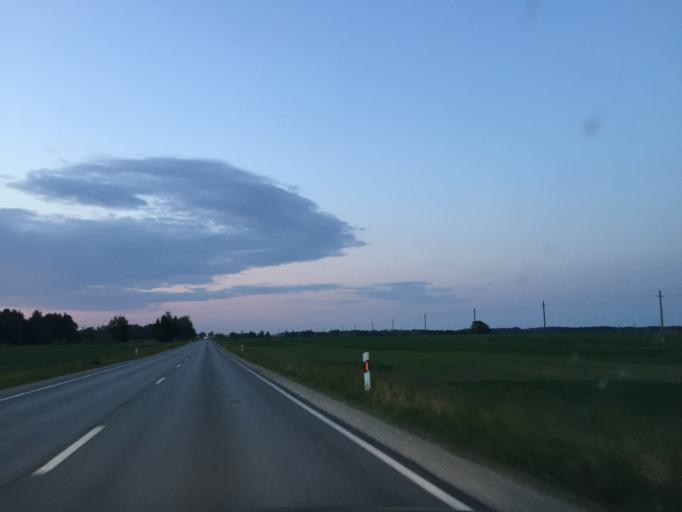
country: LT
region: Siauliu apskritis
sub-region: Joniskis
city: Joniskis
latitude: 56.1122
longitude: 23.4909
